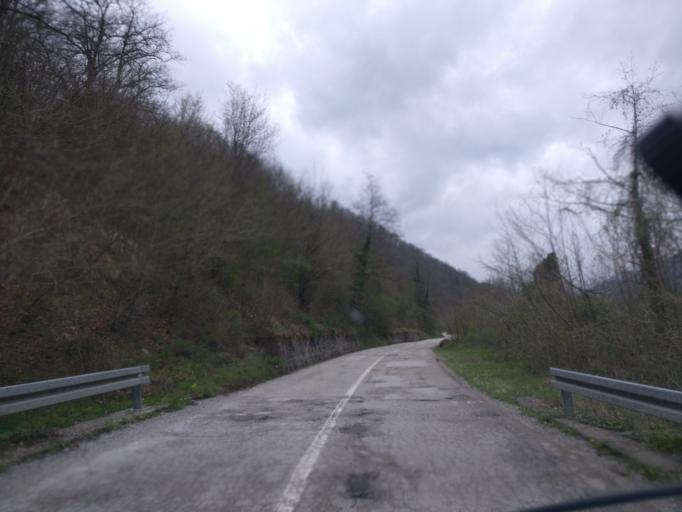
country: BA
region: Republika Srpska
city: Foca
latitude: 43.4533
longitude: 18.7537
